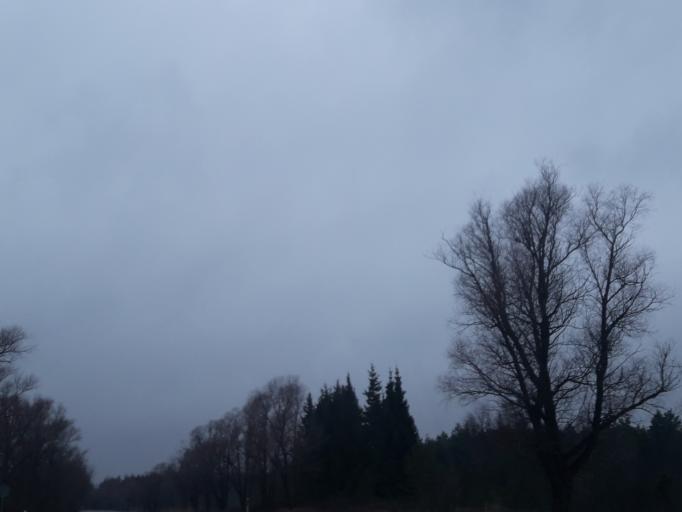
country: EE
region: Saare
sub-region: Kuressaare linn
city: Kuressaare
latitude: 58.2737
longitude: 22.4546
